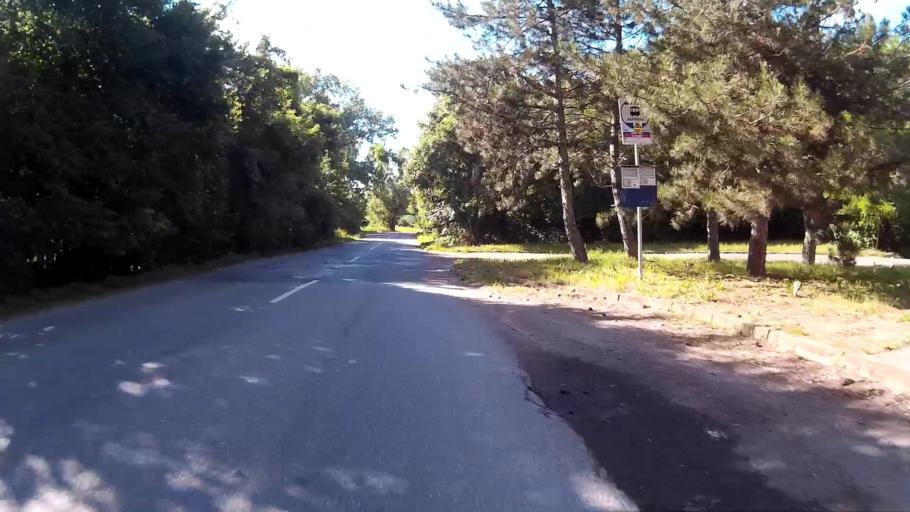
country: CZ
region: South Moravian
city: Sitborice
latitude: 48.9934
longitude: 16.7844
